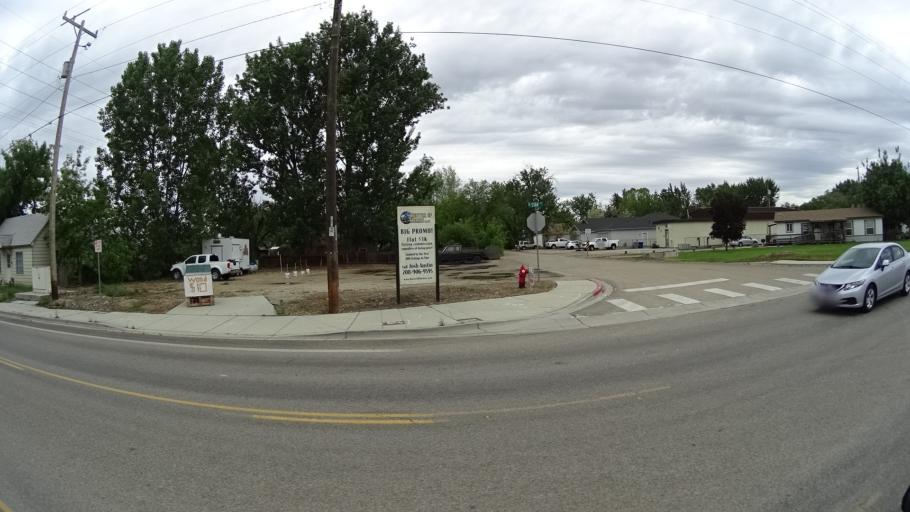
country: US
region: Idaho
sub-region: Ada County
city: Star
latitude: 43.6928
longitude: -116.4933
